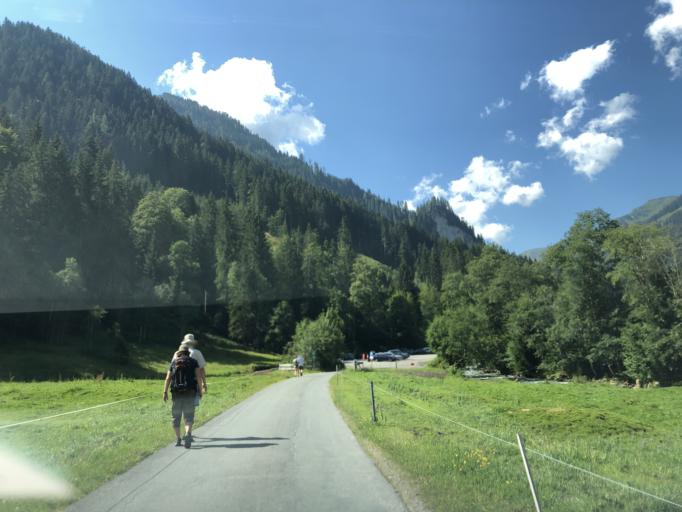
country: AT
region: Tyrol
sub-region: Politischer Bezirk Kitzbuhel
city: Kirchberg in Tirol
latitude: 47.3757
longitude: 12.3053
